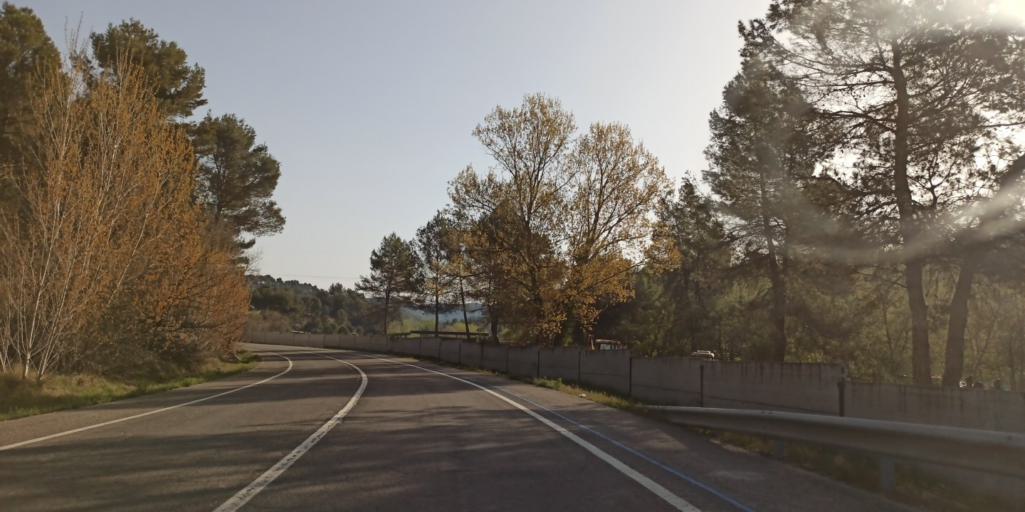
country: ES
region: Catalonia
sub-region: Provincia de Barcelona
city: Castelloli
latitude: 41.5874
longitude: 1.6808
